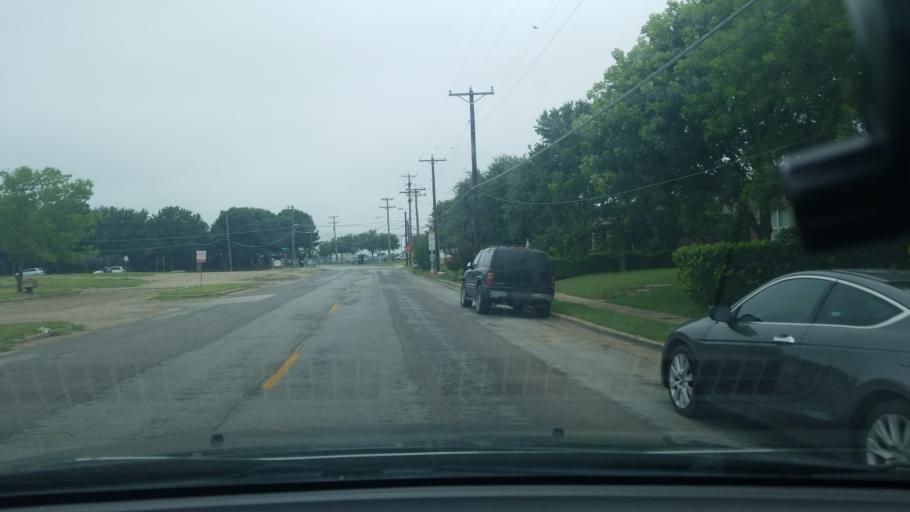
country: US
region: Texas
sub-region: Dallas County
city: Balch Springs
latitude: 32.7563
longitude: -96.6894
